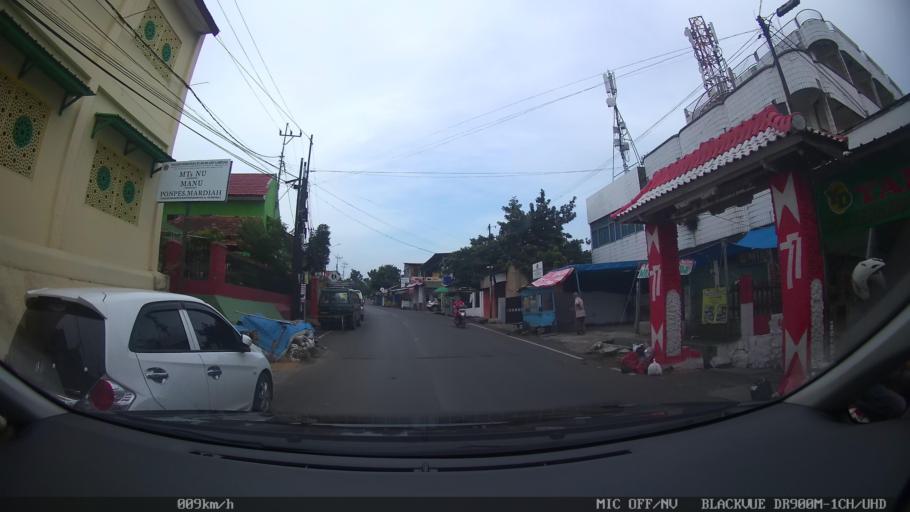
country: ID
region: Lampung
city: Bandarlampung
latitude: -5.4119
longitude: 105.2510
